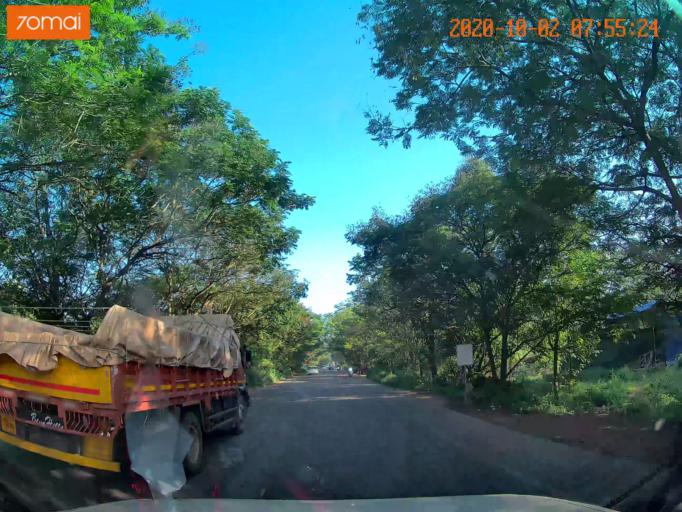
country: IN
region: Kerala
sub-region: Kozhikode
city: Ferokh
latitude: 11.1824
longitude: 75.8718
